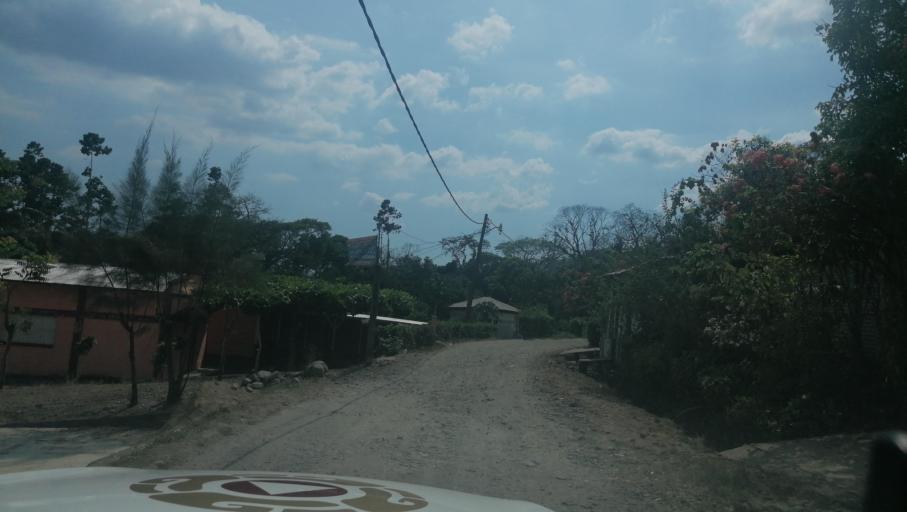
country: MX
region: Chiapas
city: Veinte de Noviembre
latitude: 15.0182
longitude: -92.2409
